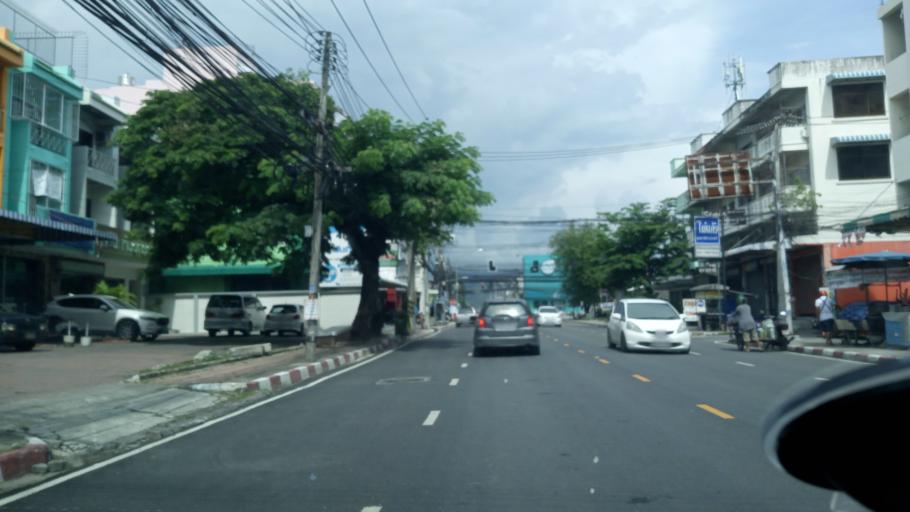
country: TH
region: Chon Buri
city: Chon Buri
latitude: 13.3234
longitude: 100.9618
